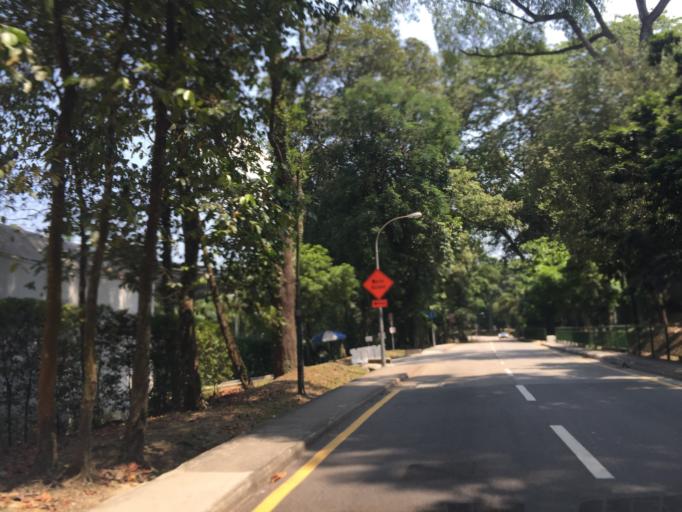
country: SG
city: Singapore
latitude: 1.3076
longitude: 103.8091
